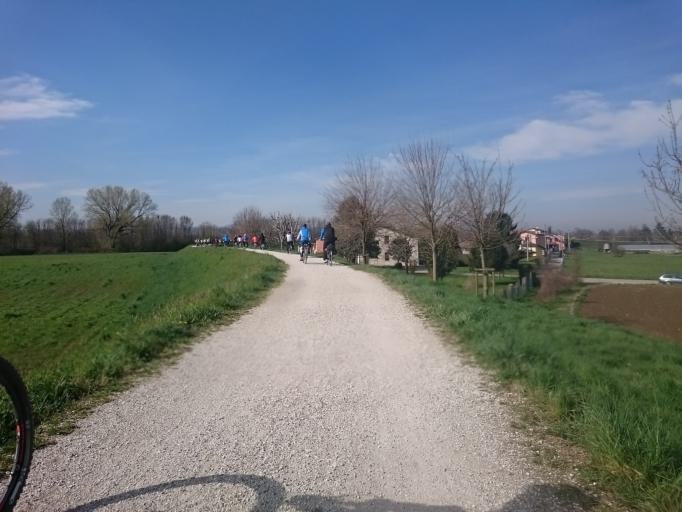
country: IT
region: Veneto
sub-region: Provincia di Padova
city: Tencarola
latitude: 45.3915
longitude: 11.8312
